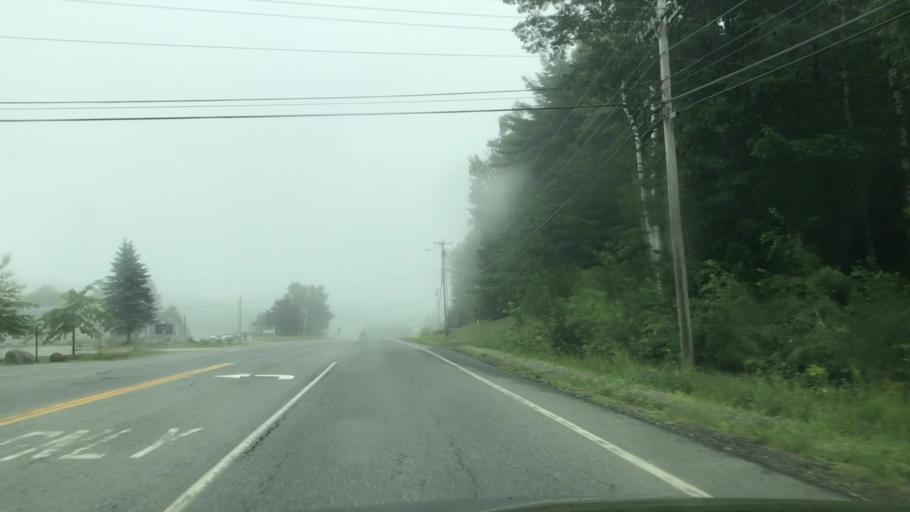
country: US
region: Maine
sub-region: Knox County
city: Rockport
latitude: 44.1862
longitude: -69.0973
